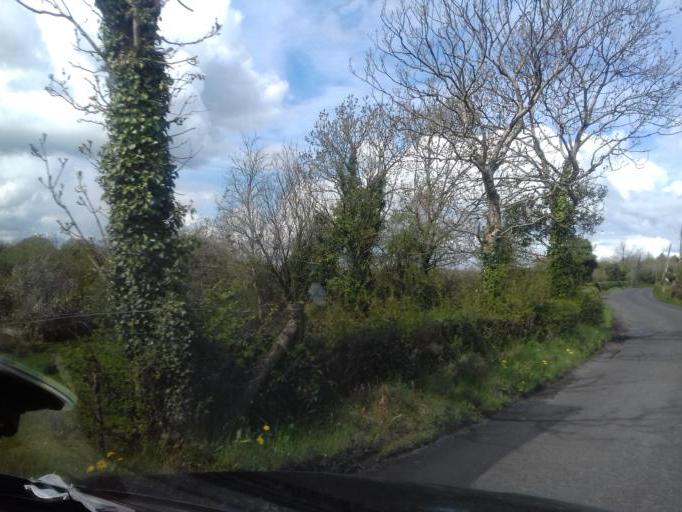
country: GB
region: Northern Ireland
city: Lisnaskea
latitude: 54.1840
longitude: -7.5017
